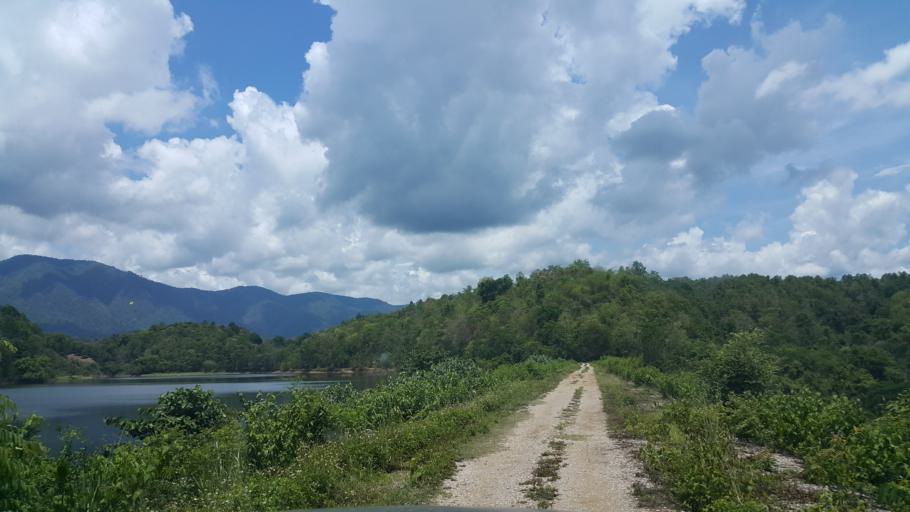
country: TH
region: Phayao
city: Phayao
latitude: 19.1846
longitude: 99.8019
